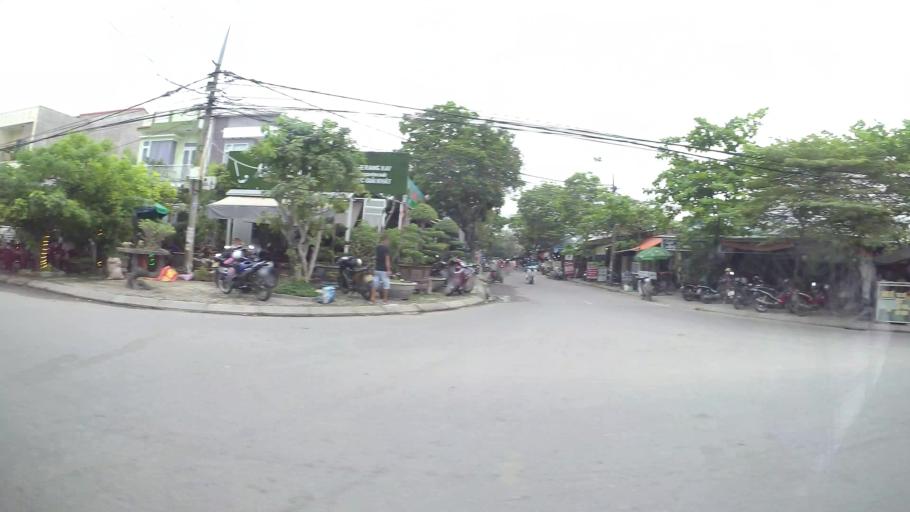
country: VN
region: Da Nang
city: Son Tra
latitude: 16.0862
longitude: 108.2430
